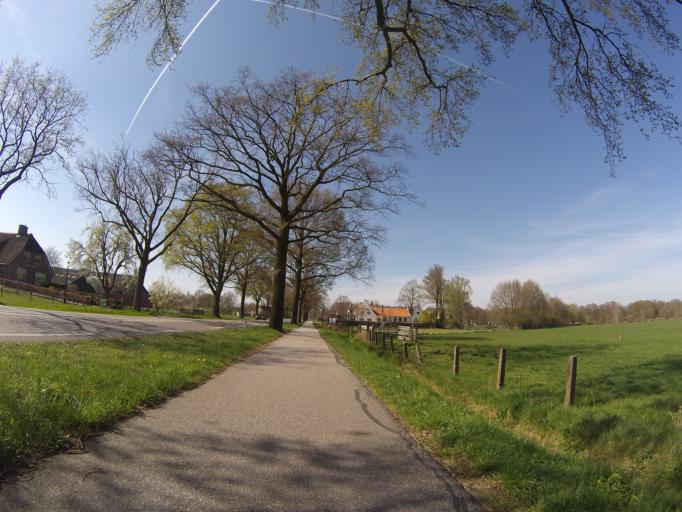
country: NL
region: Gelderland
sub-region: Gemeente Ede
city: Ederveen
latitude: 52.0615
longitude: 5.5562
